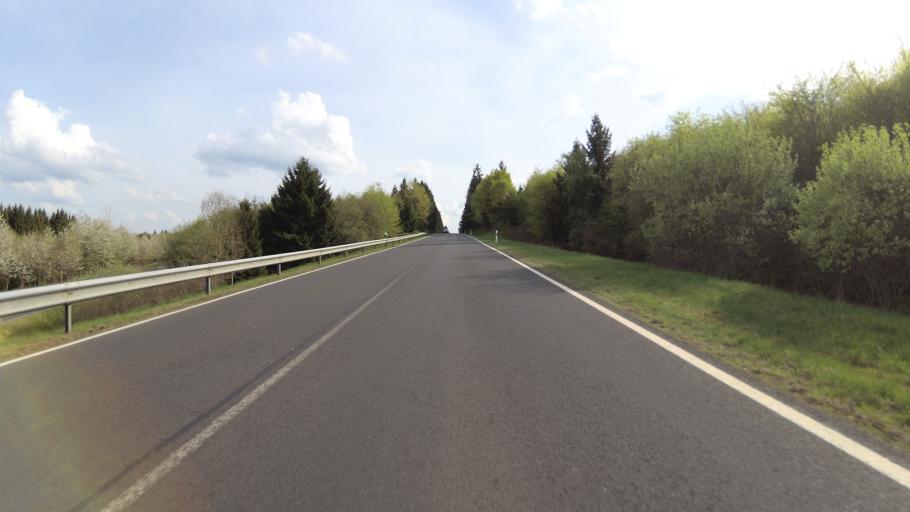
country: DE
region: Rheinland-Pfalz
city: Kelberg
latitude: 50.2730
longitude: 6.9196
